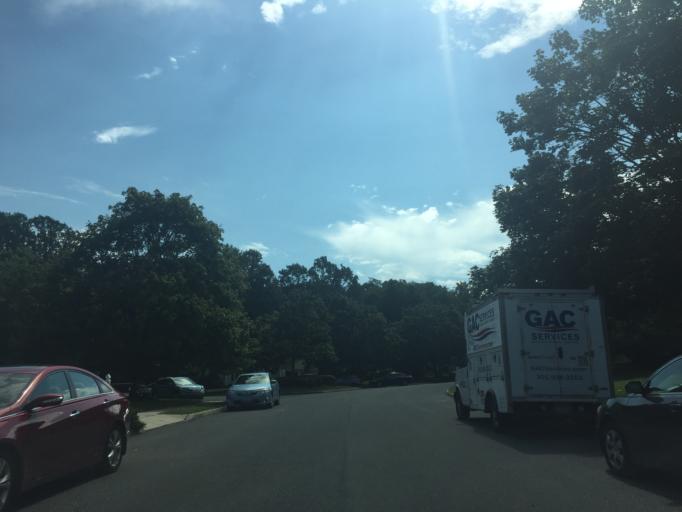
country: US
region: Maryland
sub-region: Carroll County
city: Mount Airy
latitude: 39.3786
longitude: -77.1628
